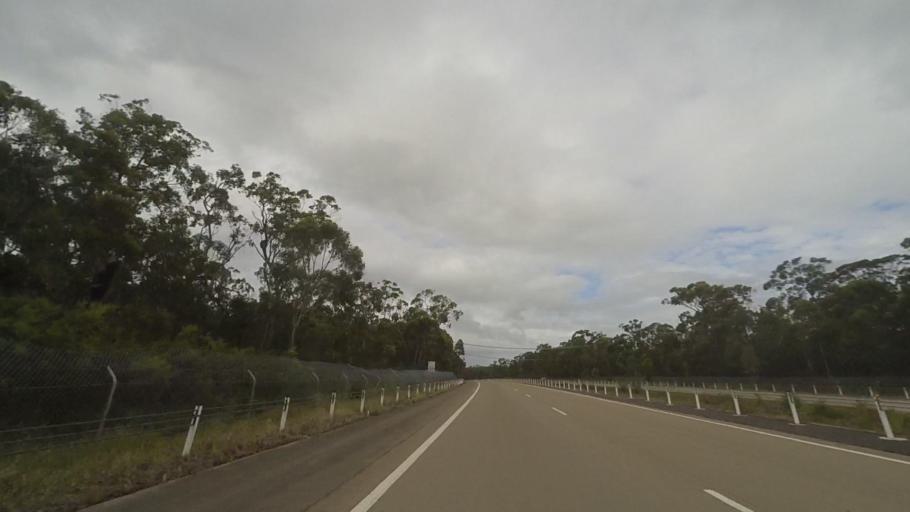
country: AU
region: New South Wales
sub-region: Port Stephens Shire
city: Medowie
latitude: -32.6450
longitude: 151.9250
